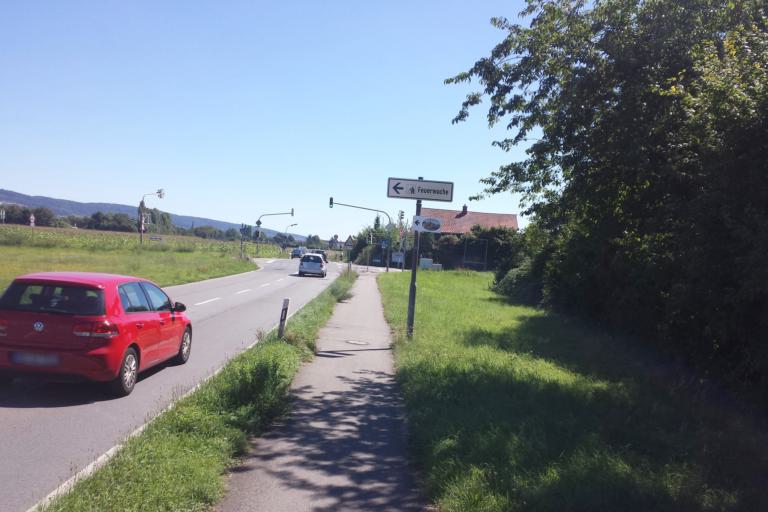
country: DE
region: Baden-Wuerttemberg
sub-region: Karlsruhe Region
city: Eppelheim
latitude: 49.3956
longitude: 8.6562
